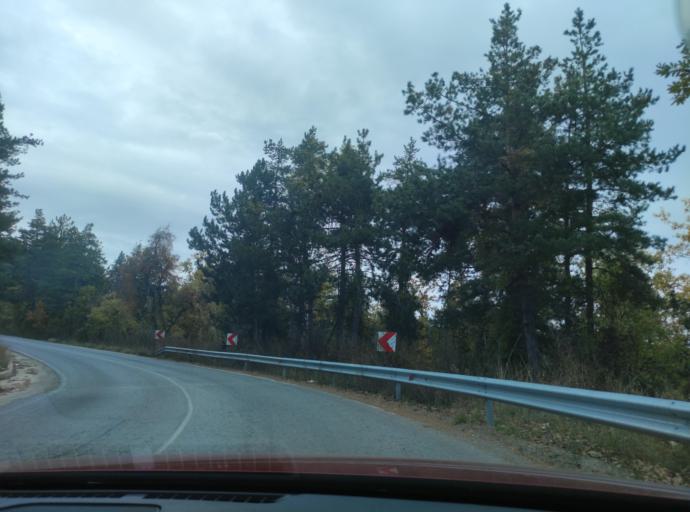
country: BG
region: Sofiya
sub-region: Obshtina Godech
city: Godech
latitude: 43.0116
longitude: 23.1217
